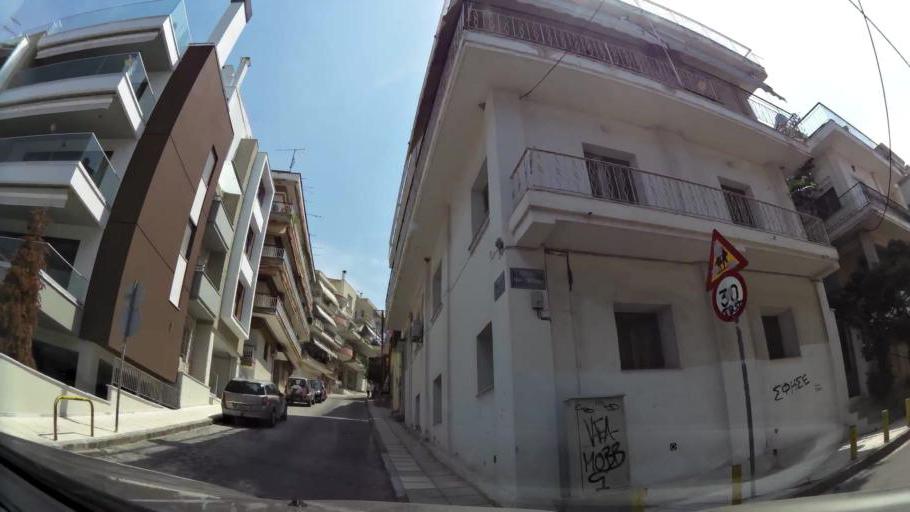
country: GR
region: Central Macedonia
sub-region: Nomos Thessalonikis
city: Agios Pavlos
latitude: 40.6299
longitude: 22.9677
